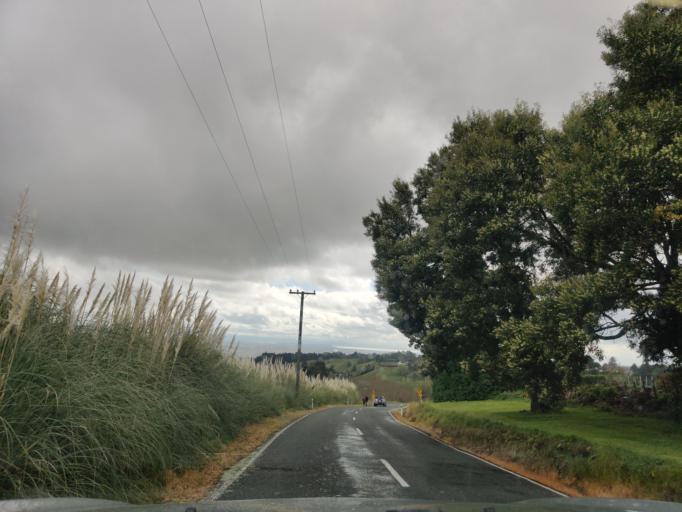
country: NZ
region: Hawke's Bay
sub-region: Hastings District
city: Hastings
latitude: -39.6908
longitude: 176.9004
